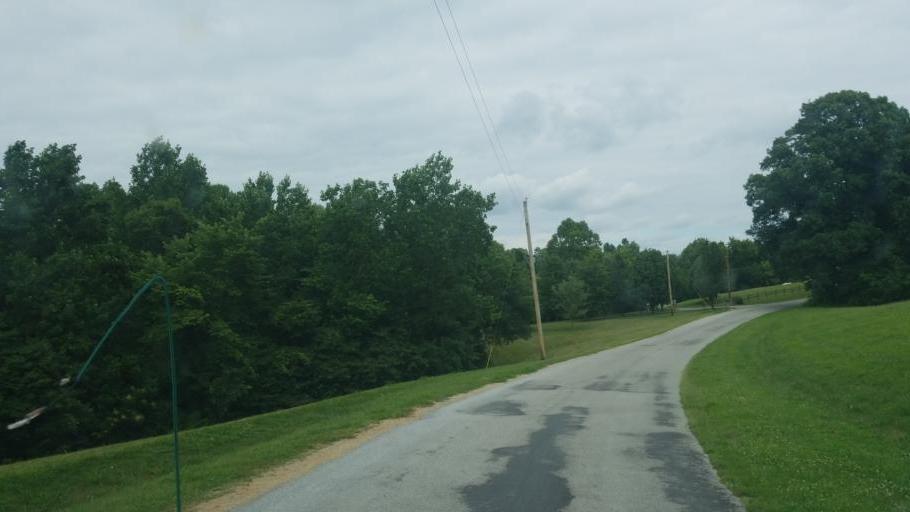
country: US
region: Illinois
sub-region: Jackson County
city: Murphysboro
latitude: 37.6723
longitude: -89.3887
